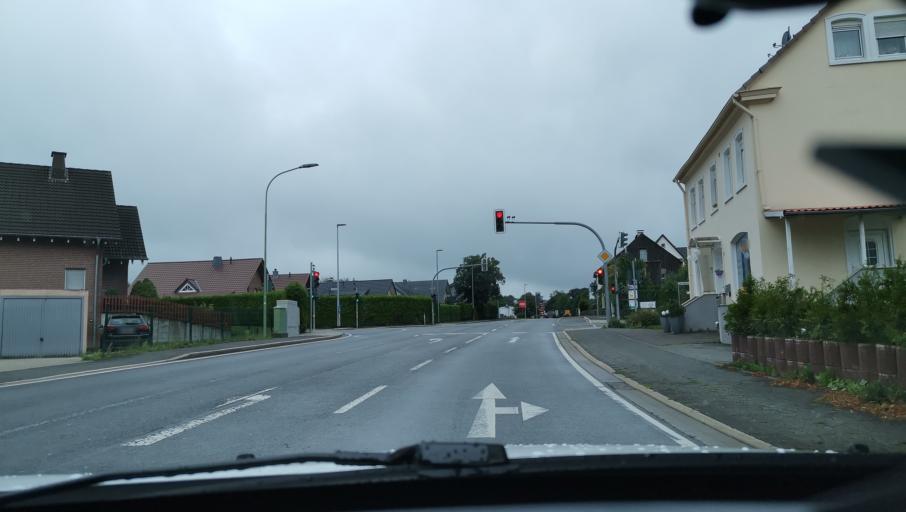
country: DE
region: North Rhine-Westphalia
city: Halver
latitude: 51.1938
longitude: 7.5088
